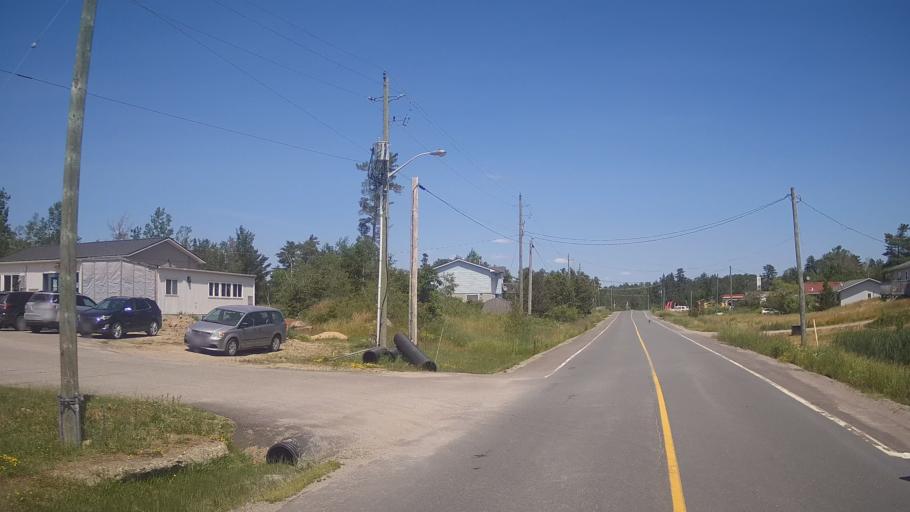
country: CA
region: Ontario
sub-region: Parry Sound District
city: Parry Sound
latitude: 45.7690
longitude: -80.5004
